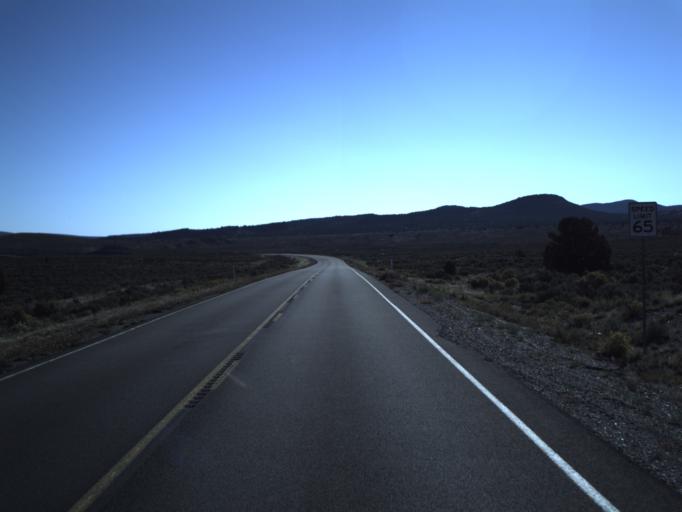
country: US
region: Utah
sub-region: Washington County
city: Enterprise
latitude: 37.7239
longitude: -114.0500
